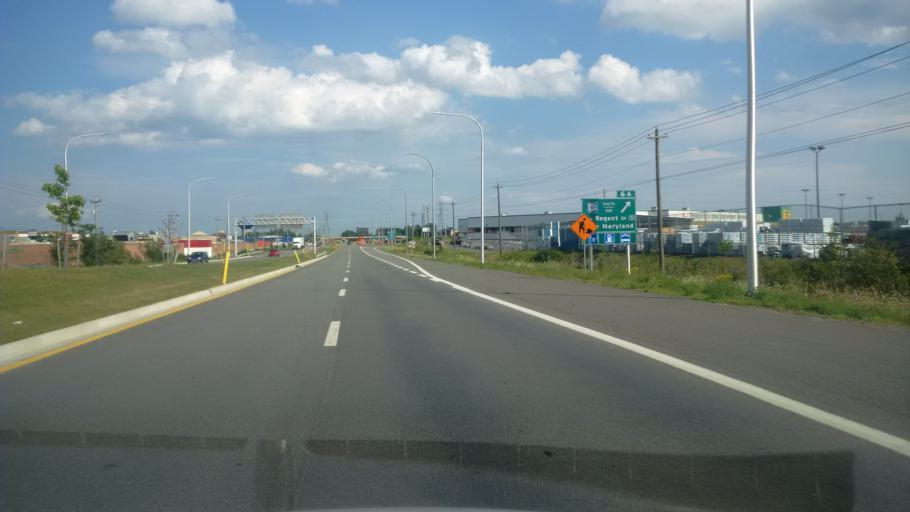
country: CA
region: New Brunswick
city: Fredericton
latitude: 45.9406
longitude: -66.6692
